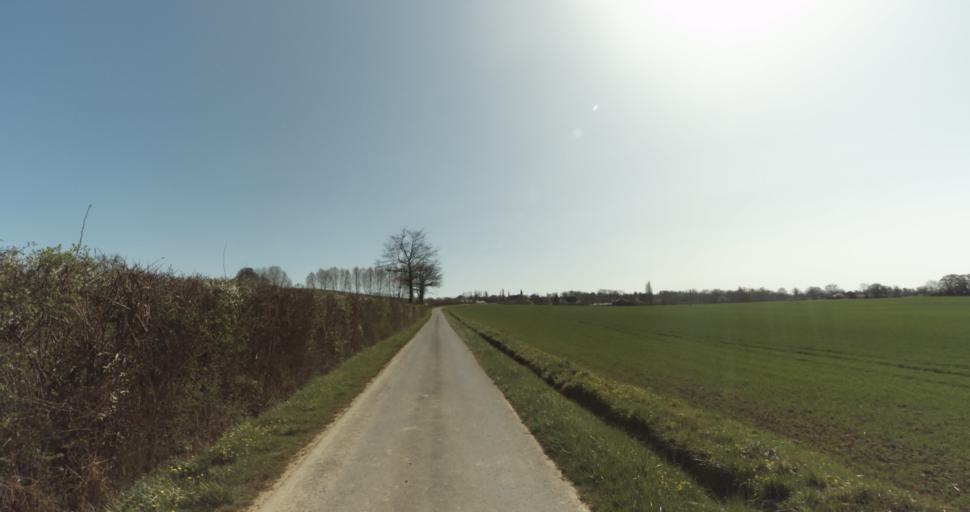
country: FR
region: Lower Normandy
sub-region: Departement du Calvados
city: Saint-Pierre-sur-Dives
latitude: 48.9518
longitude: -0.0041
